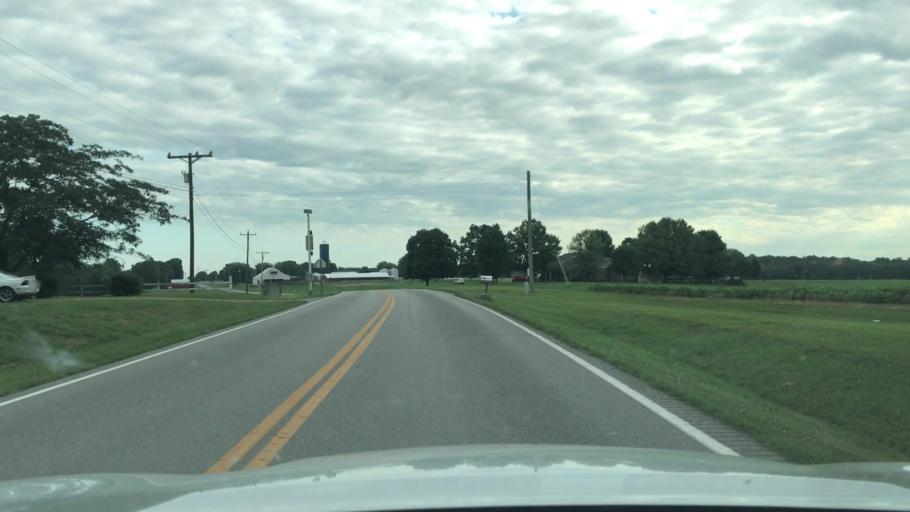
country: US
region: Kentucky
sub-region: Todd County
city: Elkton
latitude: 36.7553
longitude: -87.1680
